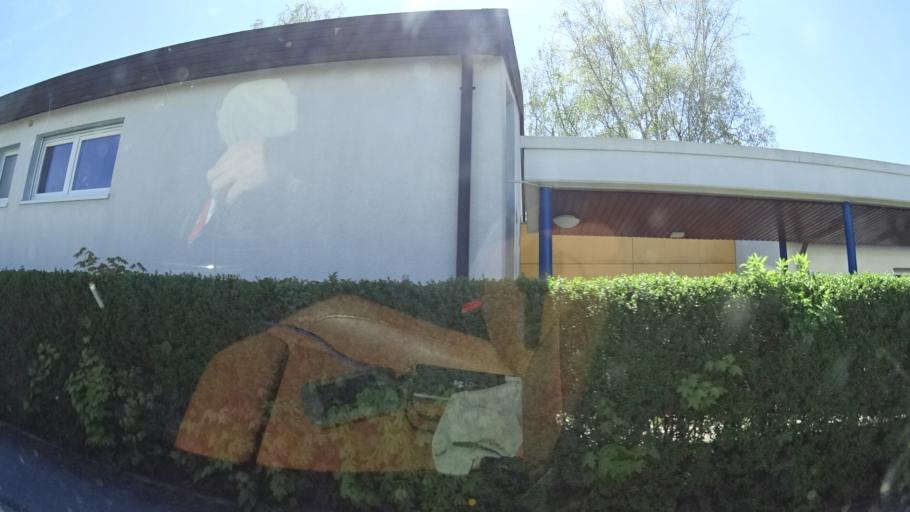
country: DE
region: Baden-Wuerttemberg
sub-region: Freiburg Region
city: Rottweil
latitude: 48.1694
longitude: 8.6127
